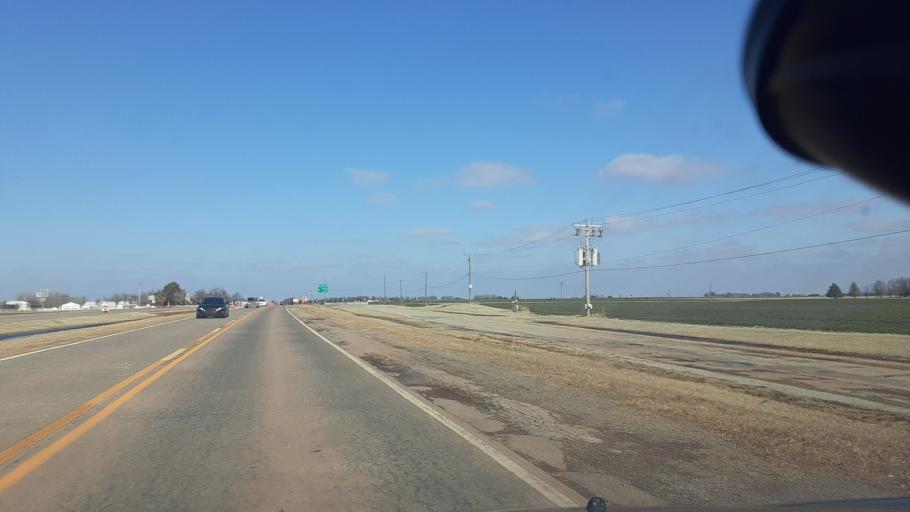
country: US
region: Oklahoma
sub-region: Garfield County
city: Enid
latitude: 36.4603
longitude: -97.8729
